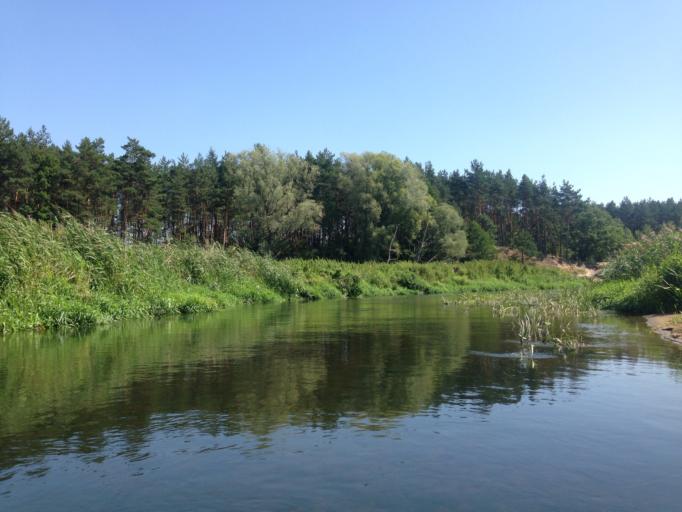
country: PL
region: Kujawsko-Pomorskie
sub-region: Powiat brodnicki
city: Bartniczka
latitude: 53.2831
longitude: 19.5614
